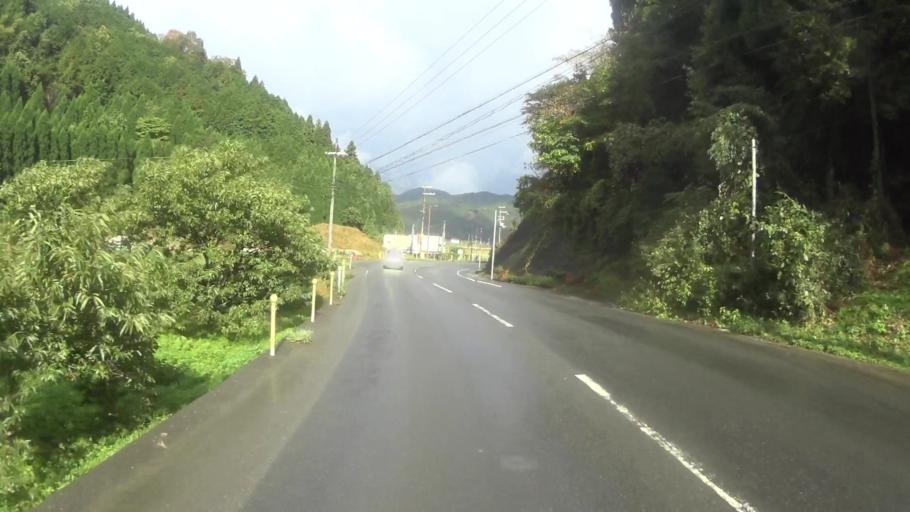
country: JP
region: Kyoto
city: Fukuchiyama
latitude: 35.3829
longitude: 135.1789
